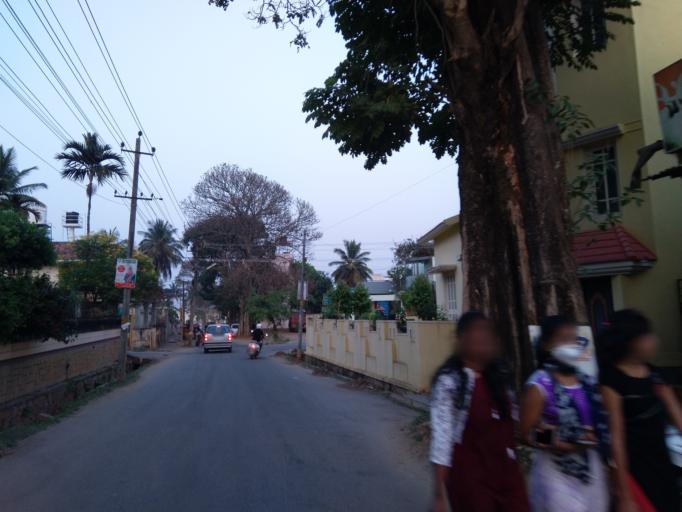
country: IN
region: Karnataka
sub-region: Hassan
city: Hassan
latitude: 13.0113
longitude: 76.1068
